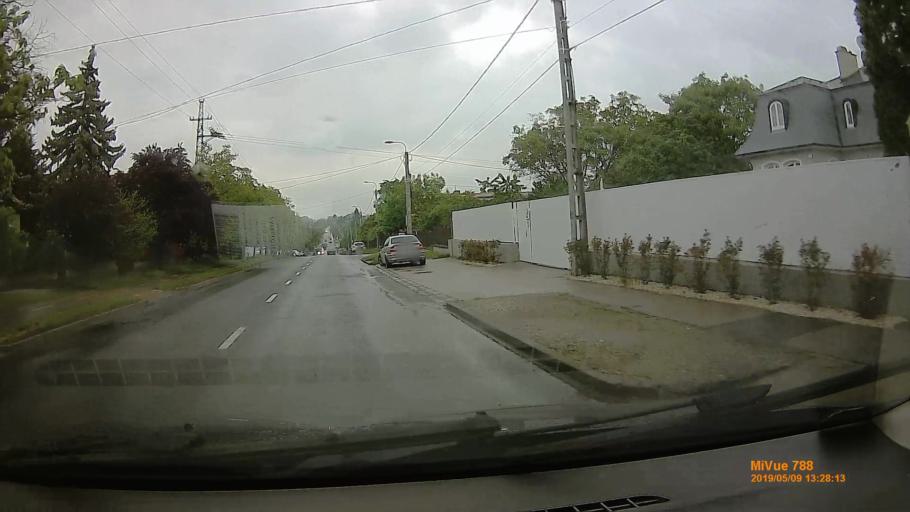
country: HU
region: Budapest
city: Budapest XVI. keruelet
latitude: 47.5343
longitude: 19.1949
